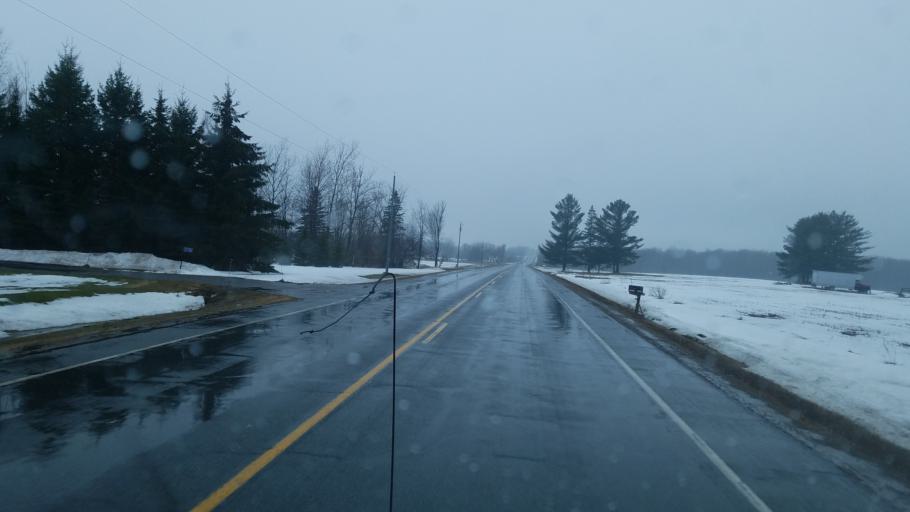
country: US
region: Wisconsin
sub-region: Marathon County
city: Spencer
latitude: 44.6777
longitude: -90.2722
